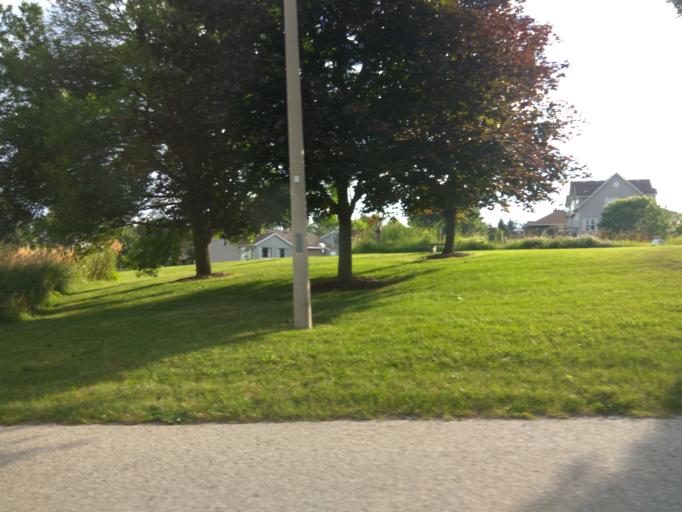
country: CA
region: Ontario
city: Kitchener
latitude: 43.3757
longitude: -80.6895
